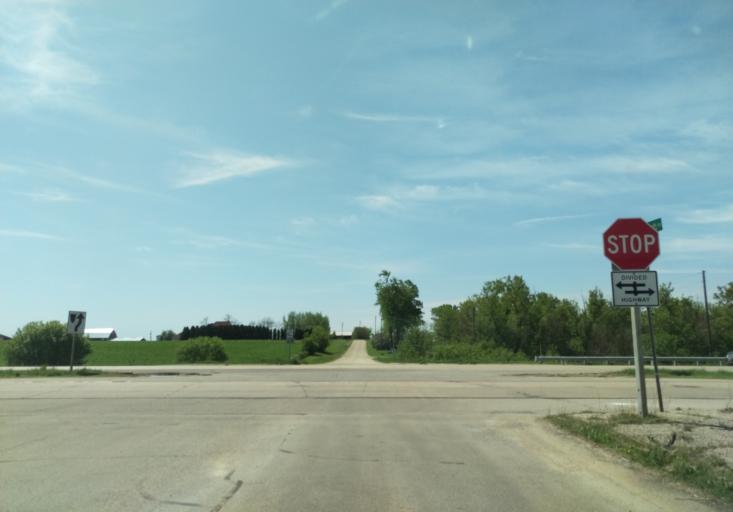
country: US
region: Wisconsin
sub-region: Dane County
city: Mount Horeb
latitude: 43.0107
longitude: -89.8097
